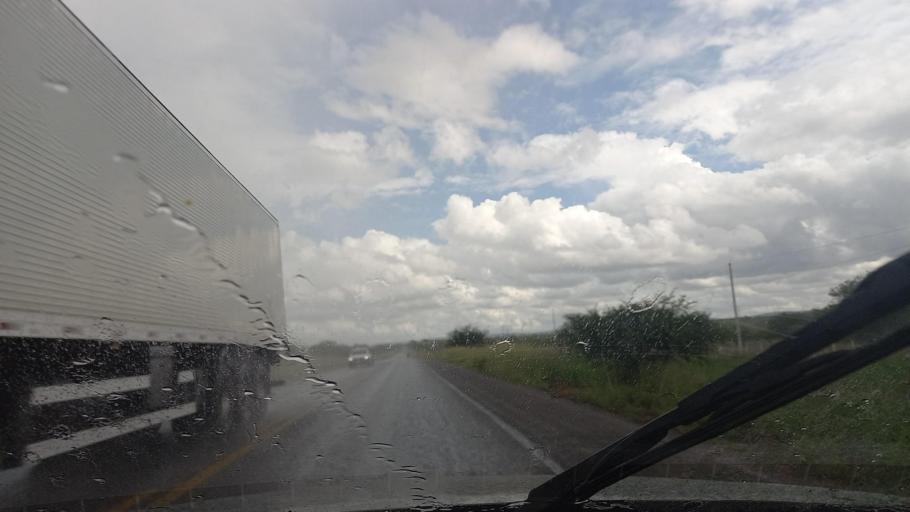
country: BR
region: Pernambuco
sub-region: Cachoeirinha
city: Cachoeirinha
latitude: -8.5510
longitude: -36.2726
